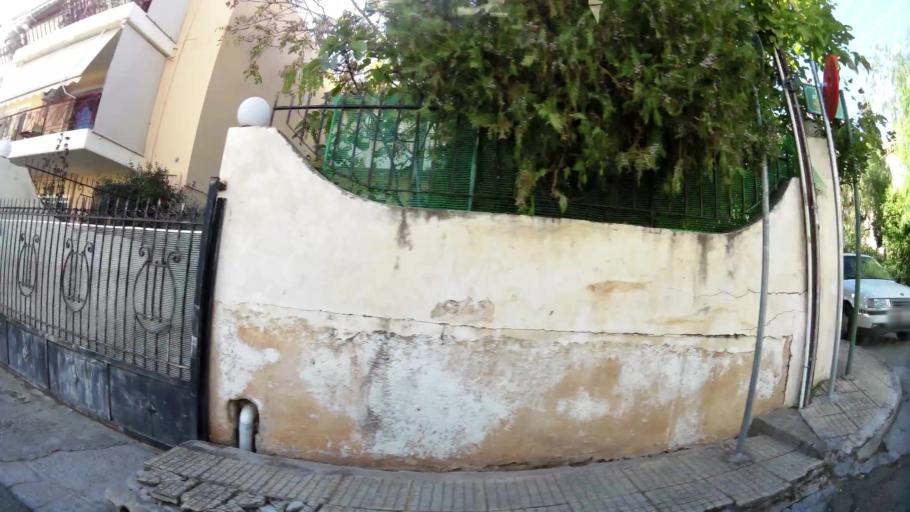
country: GR
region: Attica
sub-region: Nomarchia Anatolikis Attikis
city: Leondarion
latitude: 37.9841
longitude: 23.8452
